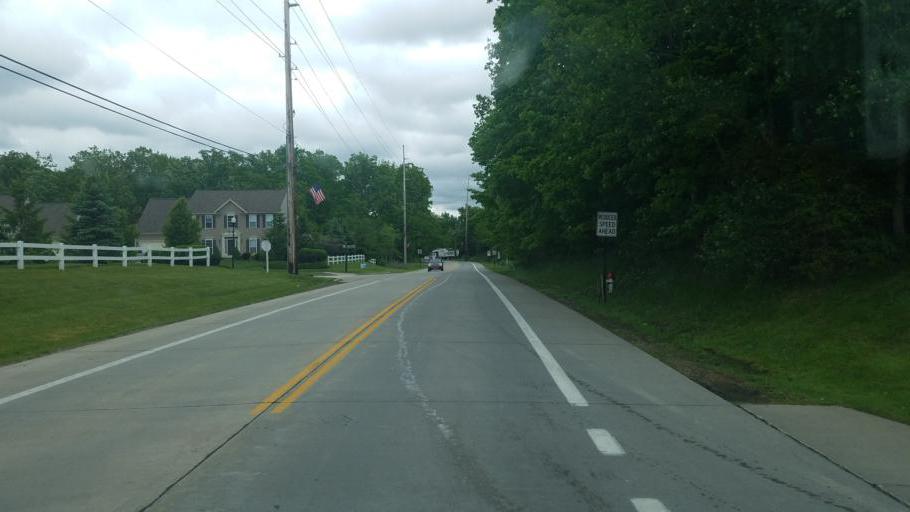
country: US
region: Ohio
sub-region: Summit County
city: Reminderville
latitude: 41.3416
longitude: -81.4085
